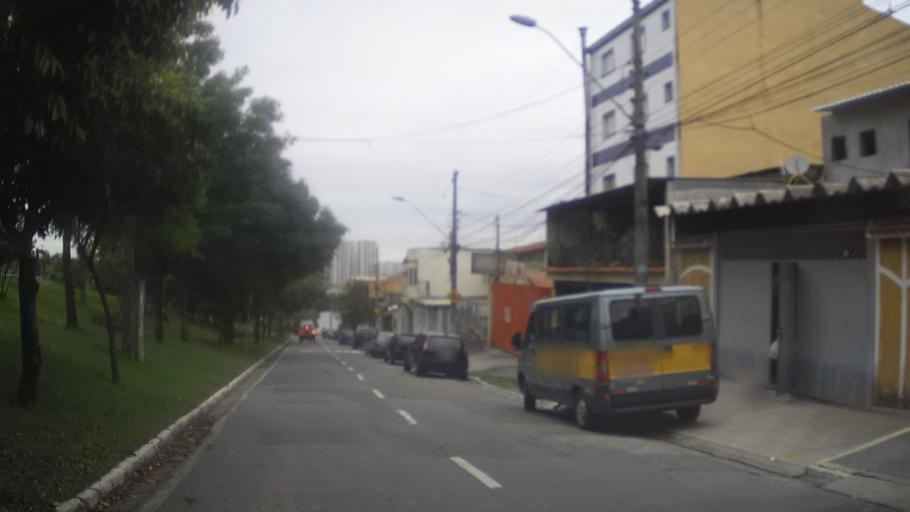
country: BR
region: Sao Paulo
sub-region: Guarulhos
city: Guarulhos
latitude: -23.4311
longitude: -46.5539
